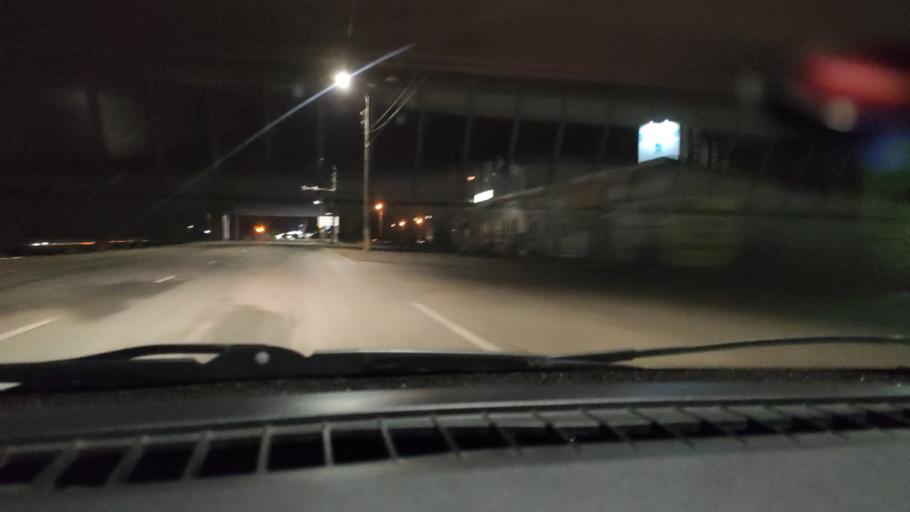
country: RU
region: Bashkortostan
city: Sterlitamak
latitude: 53.6423
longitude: 55.8965
